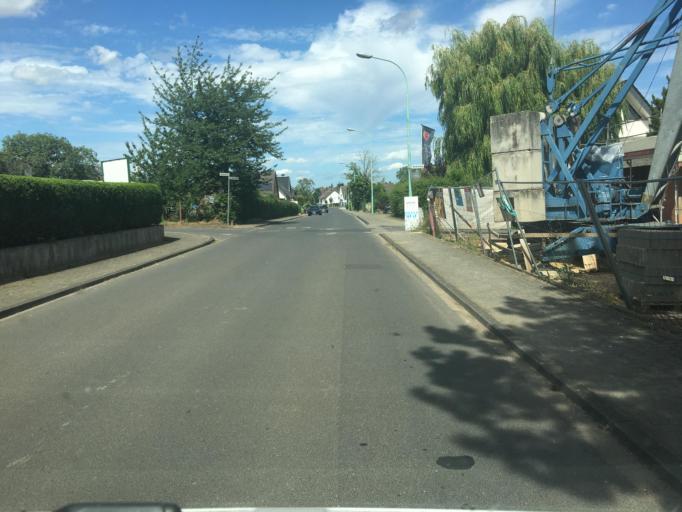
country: DE
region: North Rhine-Westphalia
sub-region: Regierungsbezirk Koln
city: Euskirchen
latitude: 50.6079
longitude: 6.8375
